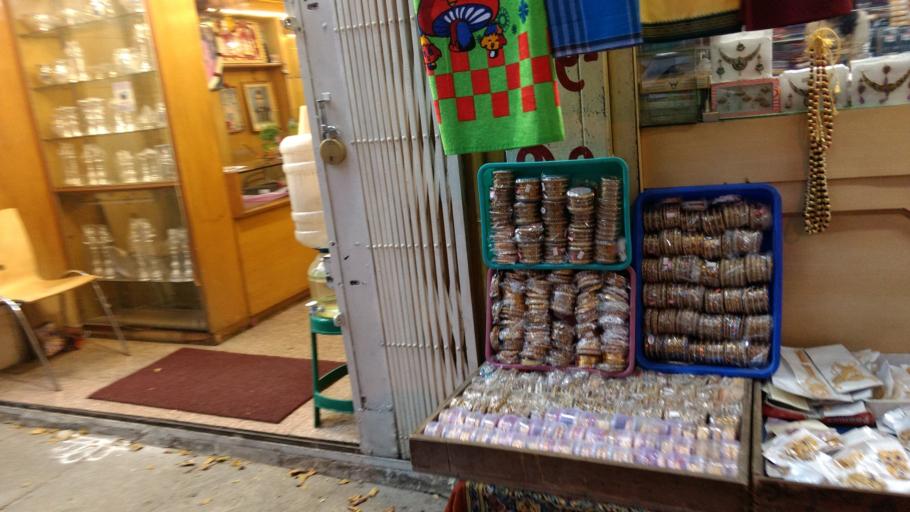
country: IN
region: Karnataka
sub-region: Bangalore Urban
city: Bangalore
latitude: 12.9997
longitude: 77.5713
